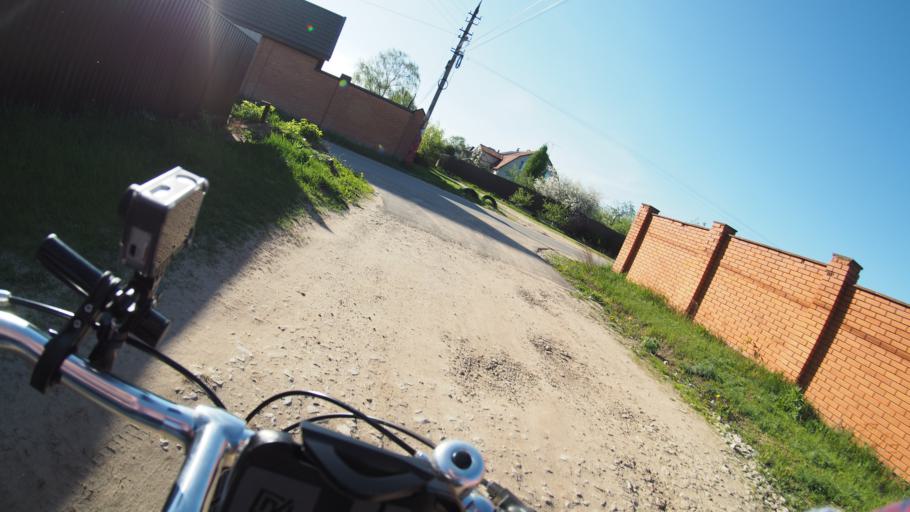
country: RU
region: Moskovskaya
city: Ramenskoye
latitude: 55.5506
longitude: 38.1928
